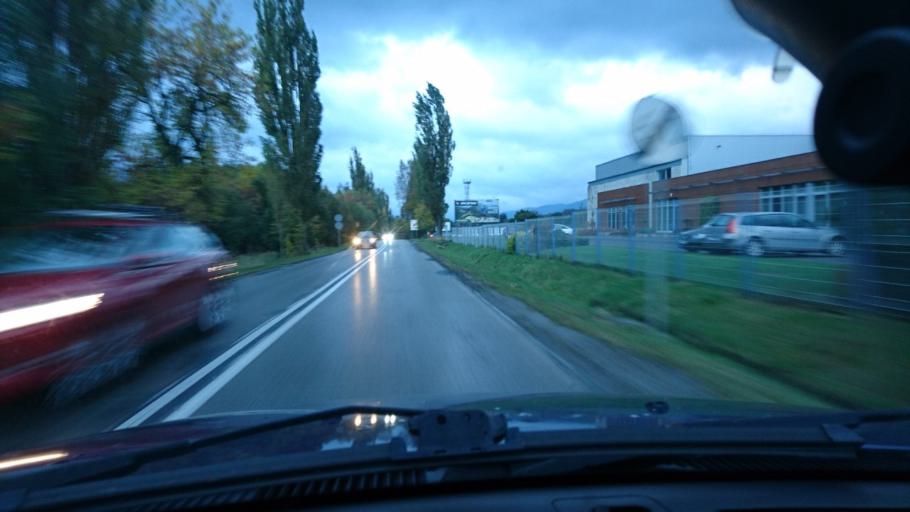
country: PL
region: Silesian Voivodeship
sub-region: Powiat bielski
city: Buczkowice
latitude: 49.7364
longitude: 19.0654
